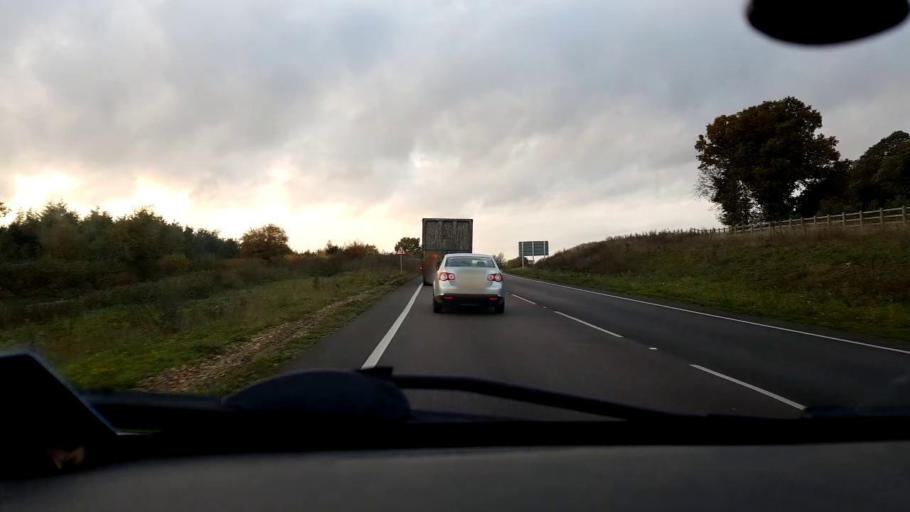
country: GB
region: England
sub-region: Norfolk
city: Costessey
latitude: 52.6941
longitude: 1.1743
